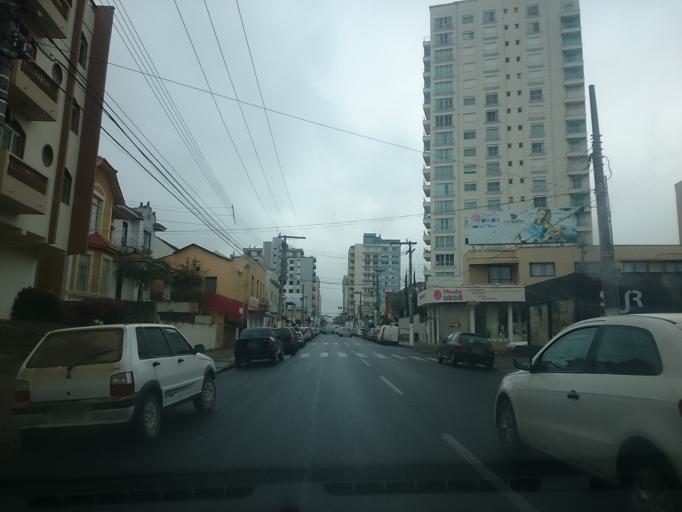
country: BR
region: Santa Catarina
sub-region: Lages
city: Lages
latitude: -27.8119
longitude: -50.3242
